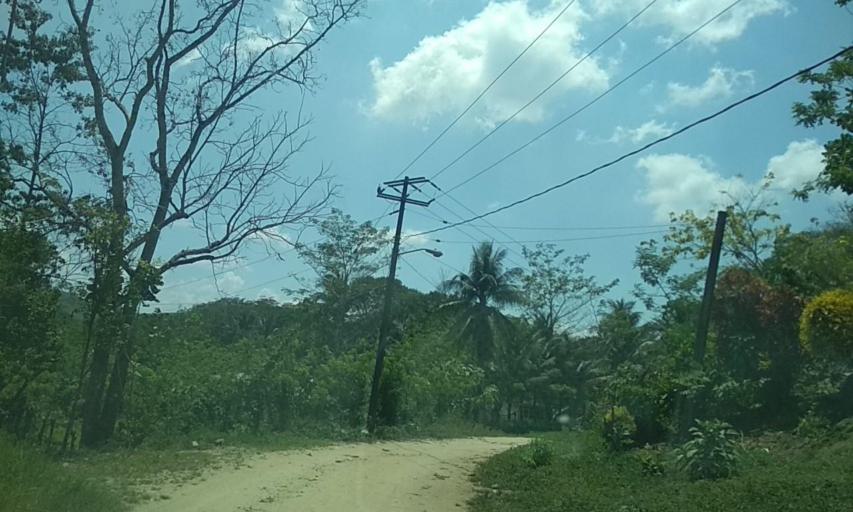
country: MX
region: Chiapas
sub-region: Tecpatan
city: Raudales Malpaso
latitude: 17.2807
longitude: -93.8274
